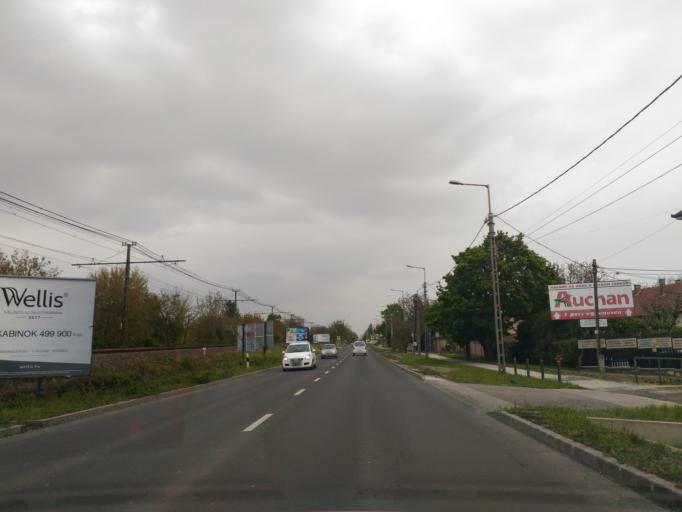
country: HU
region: Pest
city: Csomor
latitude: 47.5235
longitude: 19.2250
